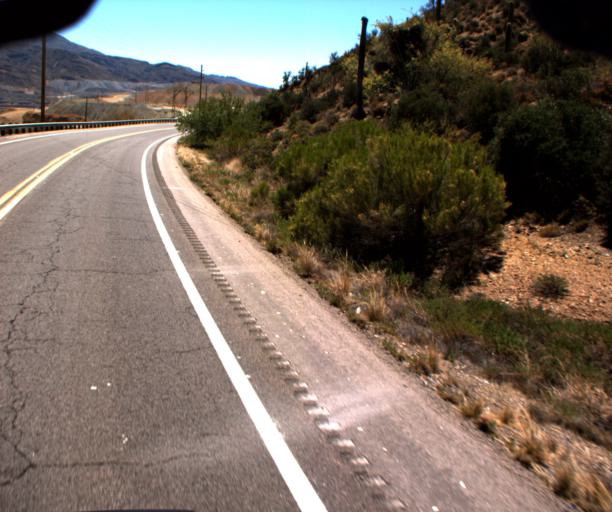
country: US
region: Arizona
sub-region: Pinal County
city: Superior
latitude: 33.1719
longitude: -111.0125
